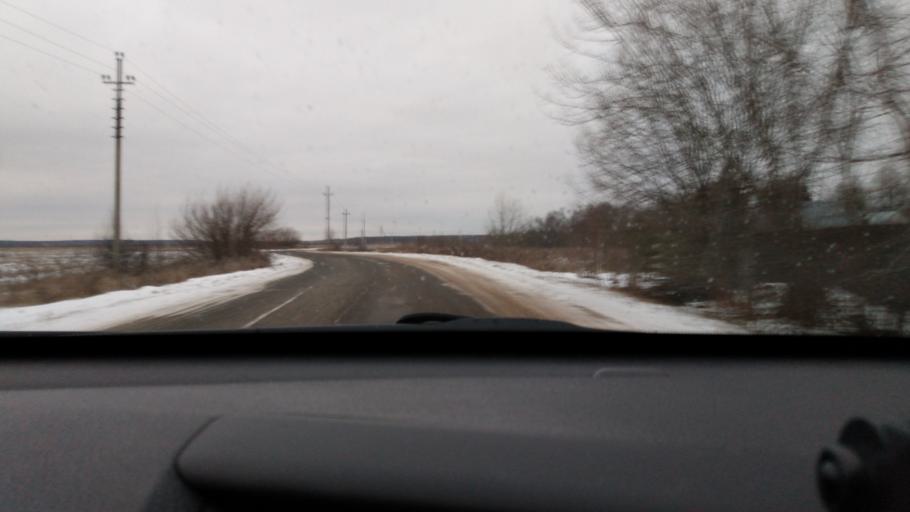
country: RU
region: Moskovskaya
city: Meshcherino
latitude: 55.2924
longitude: 38.3436
